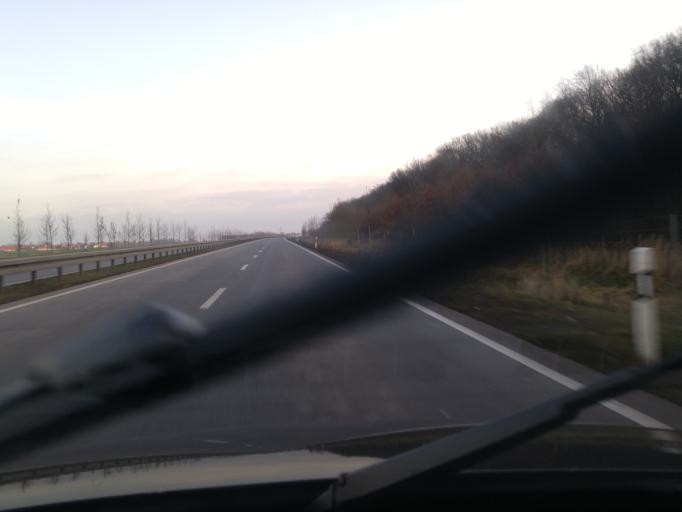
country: DE
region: Saxony
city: Rackwitz
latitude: 51.4083
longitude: 12.3221
